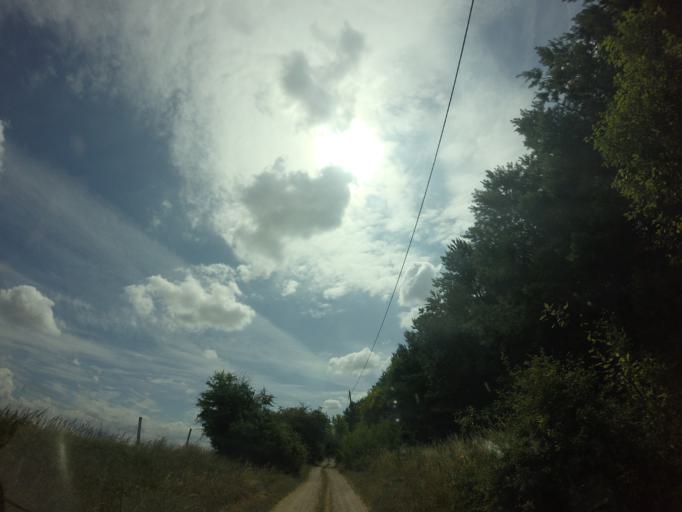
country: PL
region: West Pomeranian Voivodeship
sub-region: Powiat choszczenski
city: Drawno
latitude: 53.2016
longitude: 15.7648
